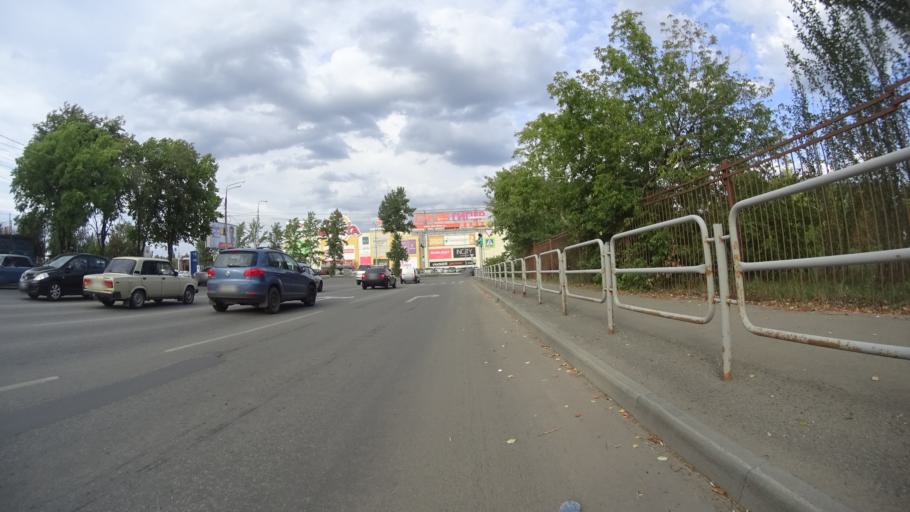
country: RU
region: Chelyabinsk
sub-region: Gorod Chelyabinsk
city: Chelyabinsk
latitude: 55.2033
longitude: 61.3236
